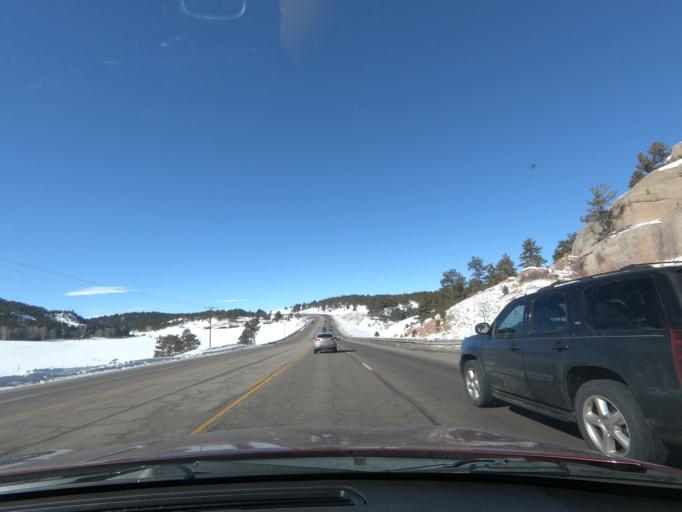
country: US
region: Colorado
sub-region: Teller County
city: Woodland Park
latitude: 38.9574
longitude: -105.1034
